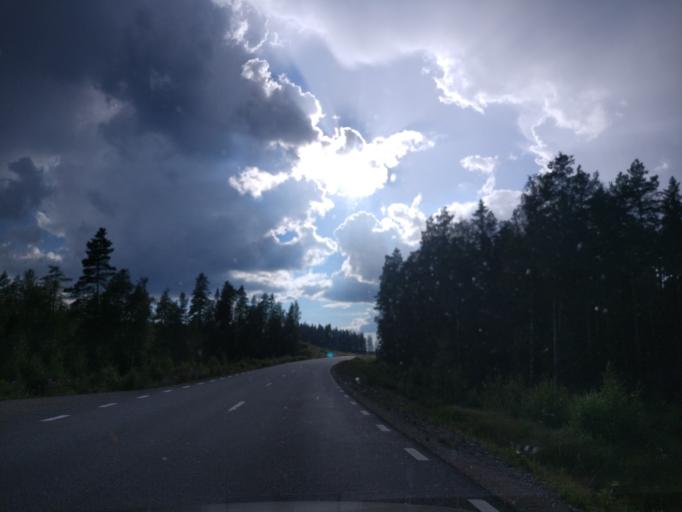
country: SE
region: Dalarna
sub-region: Ludvika Kommun
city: Abborrberget
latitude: 60.1800
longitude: 14.6983
